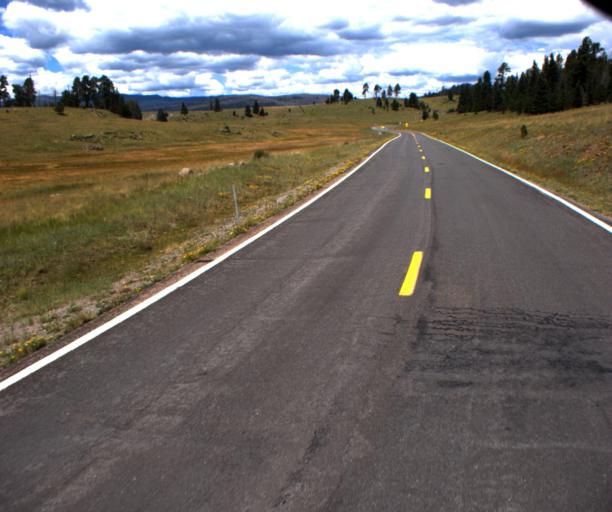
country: US
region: Arizona
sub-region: Apache County
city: Eagar
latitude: 33.8881
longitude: -109.4021
